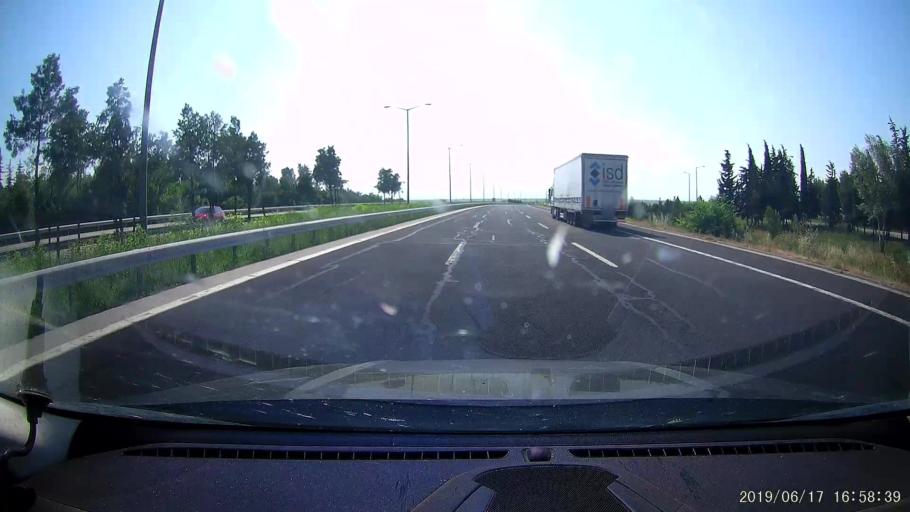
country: TR
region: Edirne
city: Haskoy
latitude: 41.6100
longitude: 26.8819
